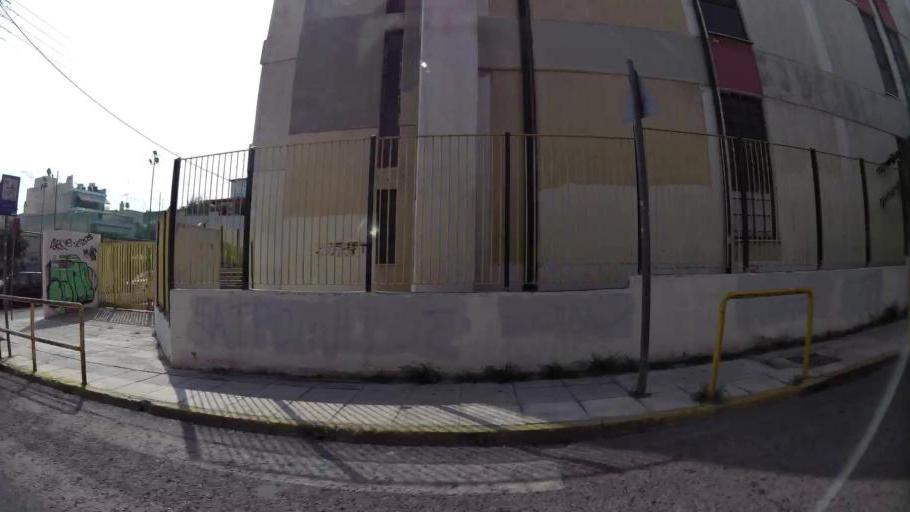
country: GR
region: Attica
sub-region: Nomarchia Athinas
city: Peristeri
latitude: 38.0148
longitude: 23.6857
